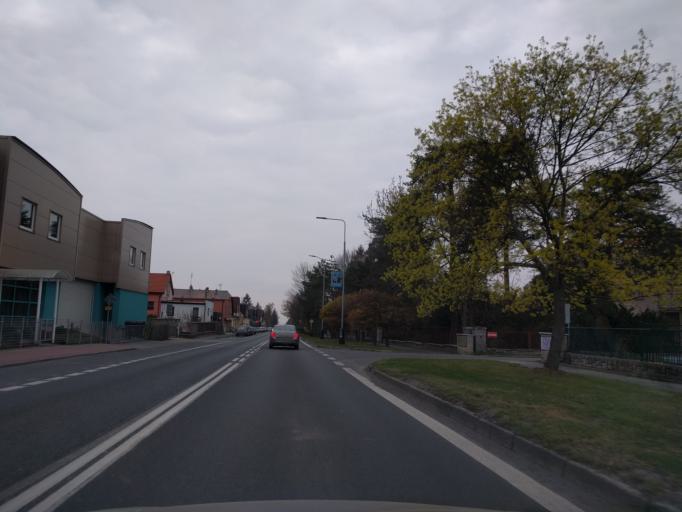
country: CZ
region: Central Bohemia
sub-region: Okres Praha-Vychod
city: Ricany
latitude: 49.9933
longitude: 14.6872
